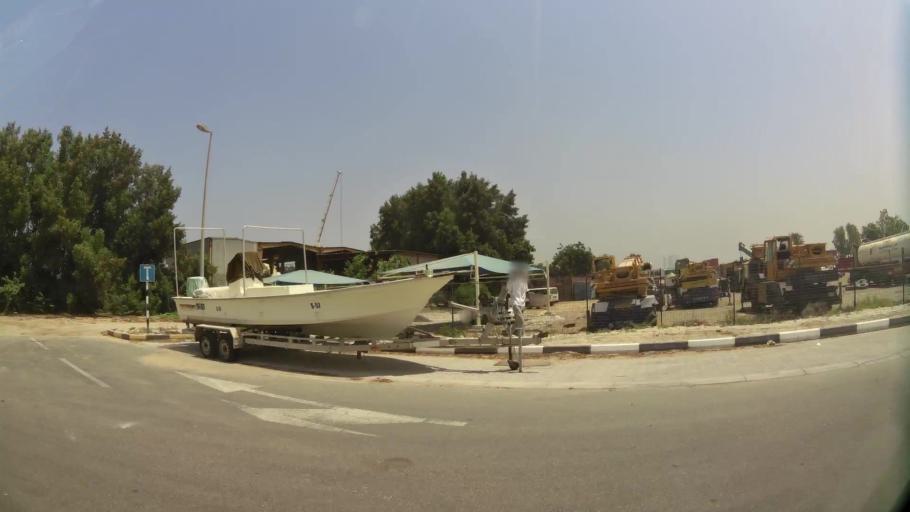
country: AE
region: Ash Shariqah
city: Sharjah
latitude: 25.3476
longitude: 55.3707
